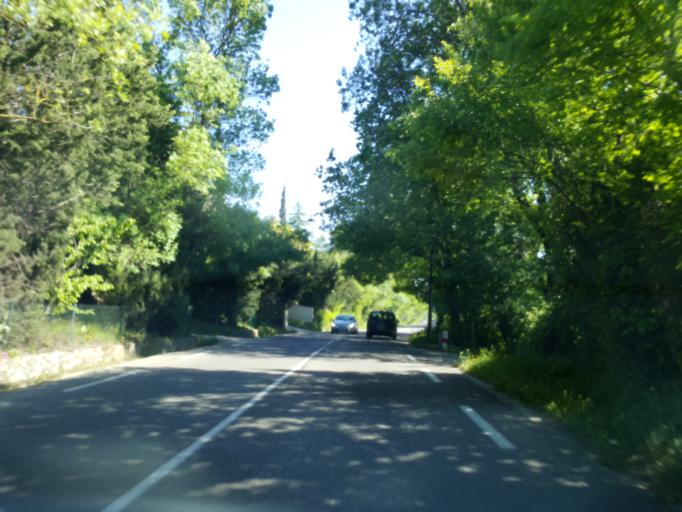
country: FR
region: Provence-Alpes-Cote d'Azur
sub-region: Departement du Var
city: Sollies-Toucas
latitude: 43.2155
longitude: 6.0259
